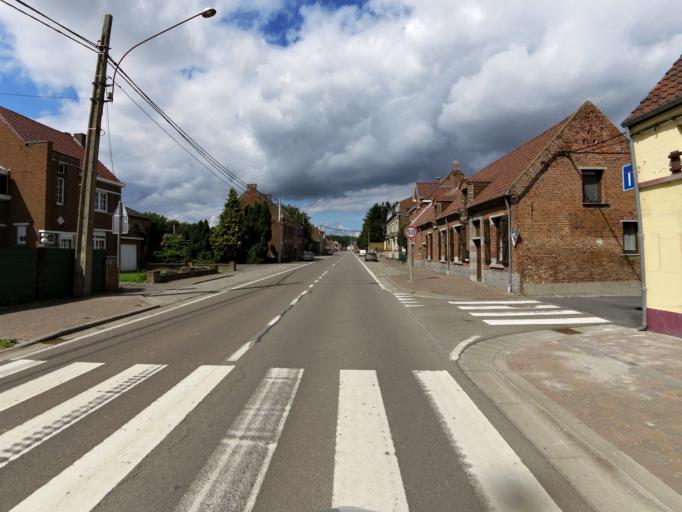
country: BE
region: Wallonia
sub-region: Province du Hainaut
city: Chasse Royale
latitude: 50.4066
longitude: 4.0168
